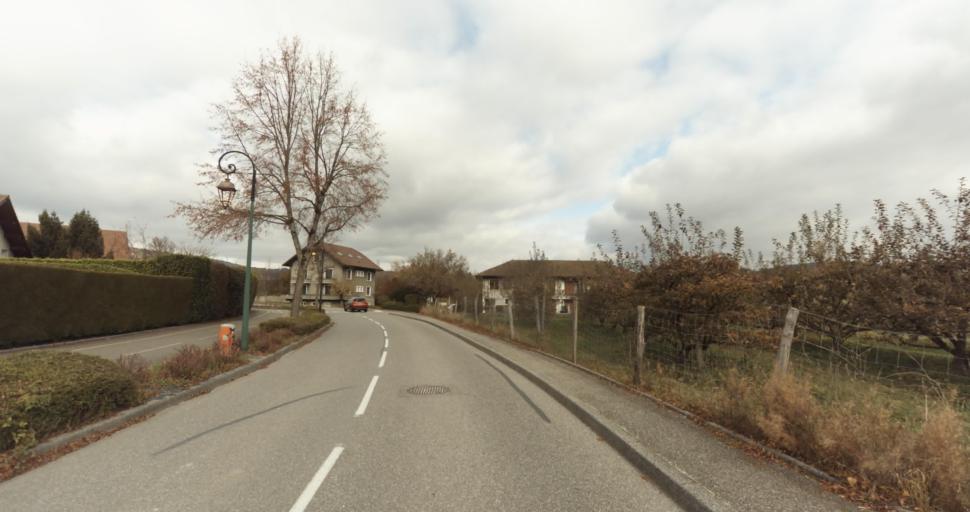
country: FR
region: Rhone-Alpes
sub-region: Departement de la Haute-Savoie
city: Metz-Tessy
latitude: 45.9364
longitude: 6.1107
